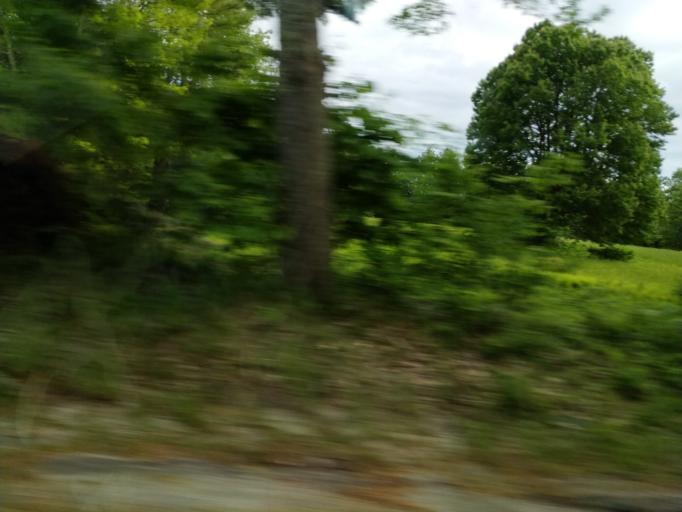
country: US
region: Maine
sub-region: Cumberland County
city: New Gloucester
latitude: 43.8859
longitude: -70.3149
